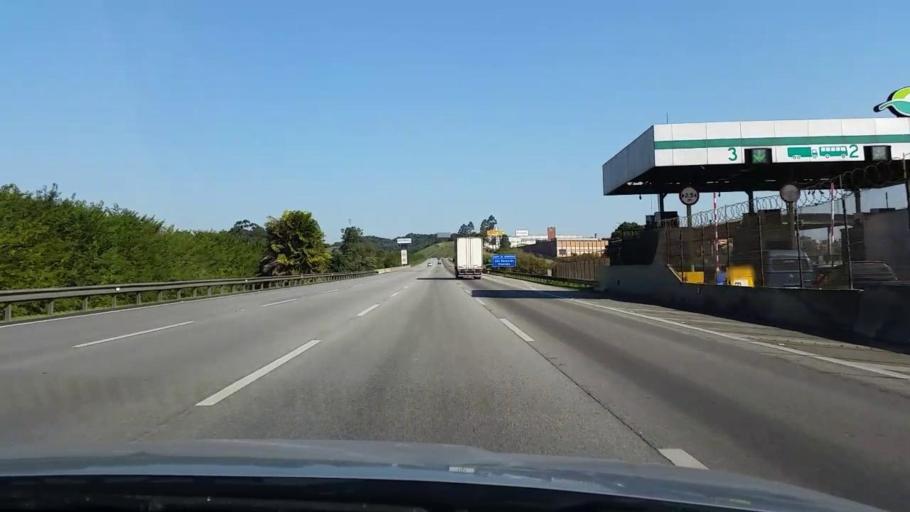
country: BR
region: Sao Paulo
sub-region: Diadema
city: Diadema
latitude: -23.7174
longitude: -46.6056
